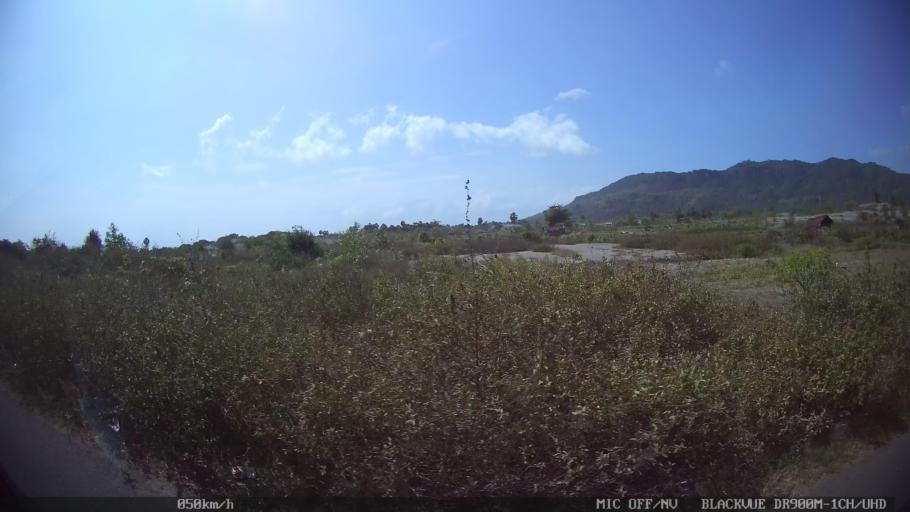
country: ID
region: Daerah Istimewa Yogyakarta
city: Bambanglipuro
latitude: -8.0172
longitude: 110.3135
